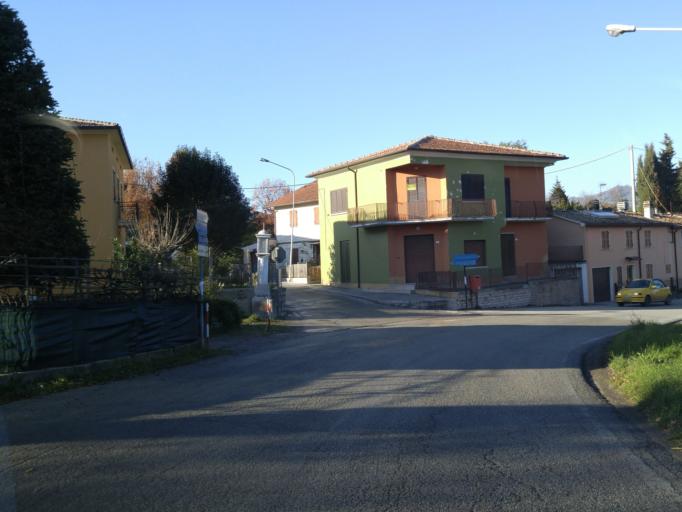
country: IT
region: The Marches
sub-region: Provincia di Pesaro e Urbino
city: Montefelcino
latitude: 43.7466
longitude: 12.8155
